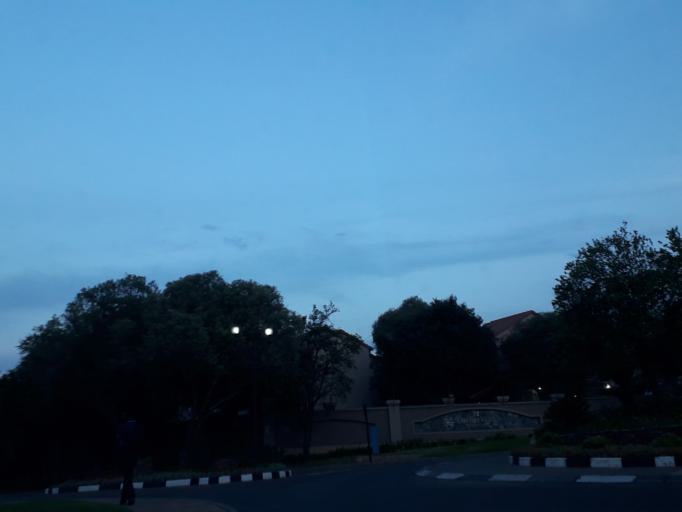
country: ZA
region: Gauteng
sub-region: City of Johannesburg Metropolitan Municipality
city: Diepsloot
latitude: -25.9911
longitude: 28.0085
